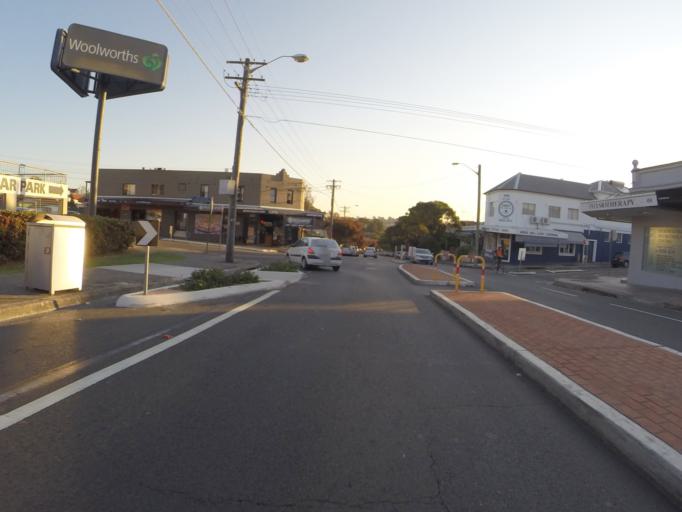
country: AU
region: New South Wales
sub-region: Marrickville
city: Marrickville
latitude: -33.9166
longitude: 151.1495
